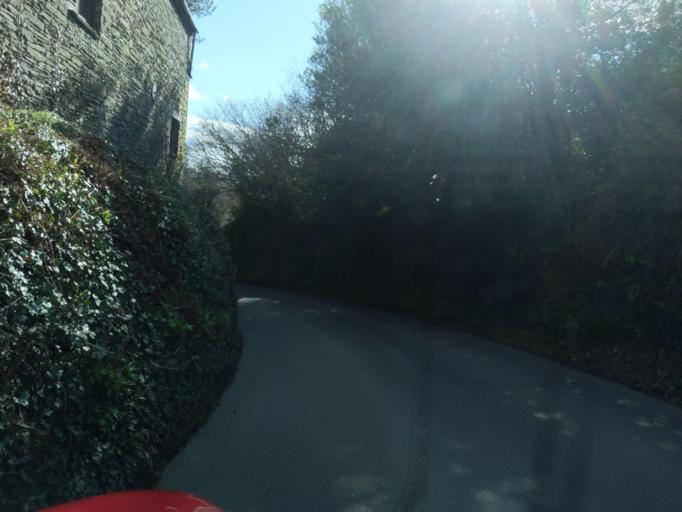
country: GB
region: England
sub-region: Devon
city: Kingsbridge
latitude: 50.2898
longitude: -3.7706
